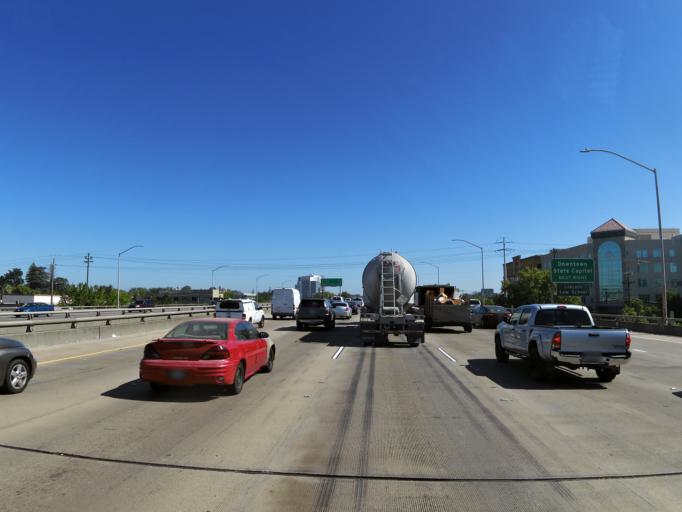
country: US
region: California
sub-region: Sacramento County
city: Sacramento
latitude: 38.5635
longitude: -121.4714
